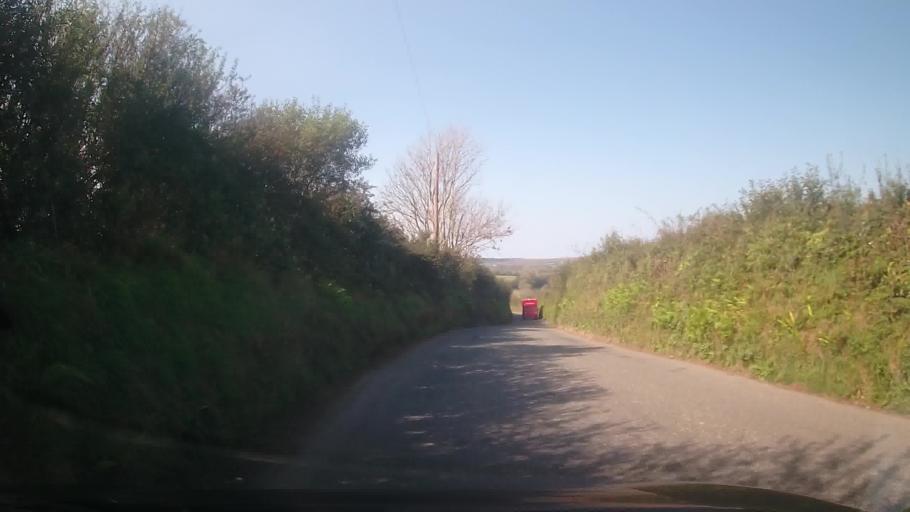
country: GB
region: Wales
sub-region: Pembrokeshire
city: Camrose
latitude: 51.8357
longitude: -4.9769
